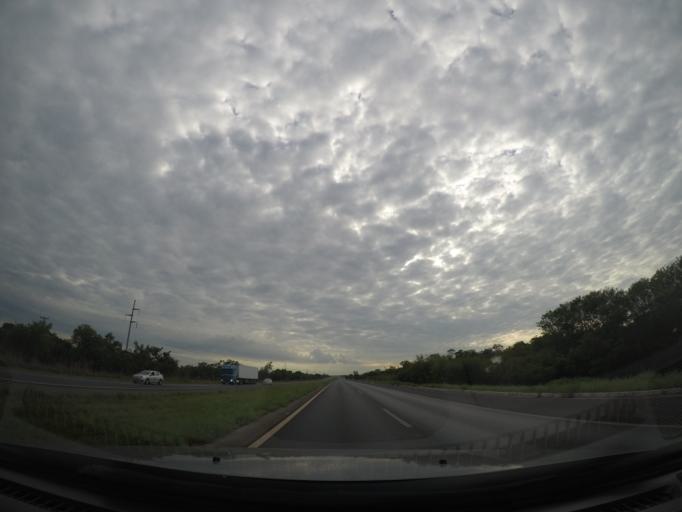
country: BR
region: Goias
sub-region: Planaltina
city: Planaltina
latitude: -15.5967
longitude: -47.6372
